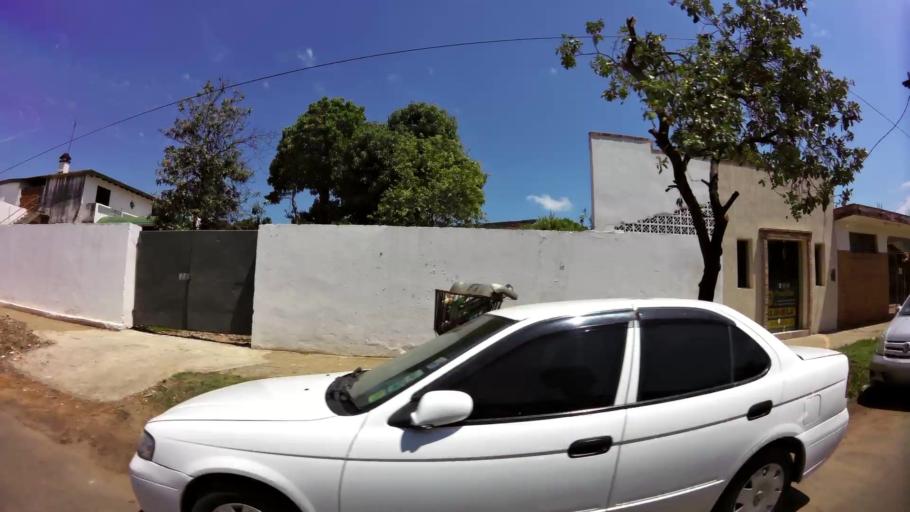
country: PY
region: Central
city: Fernando de la Mora
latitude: -25.3269
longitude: -57.5502
